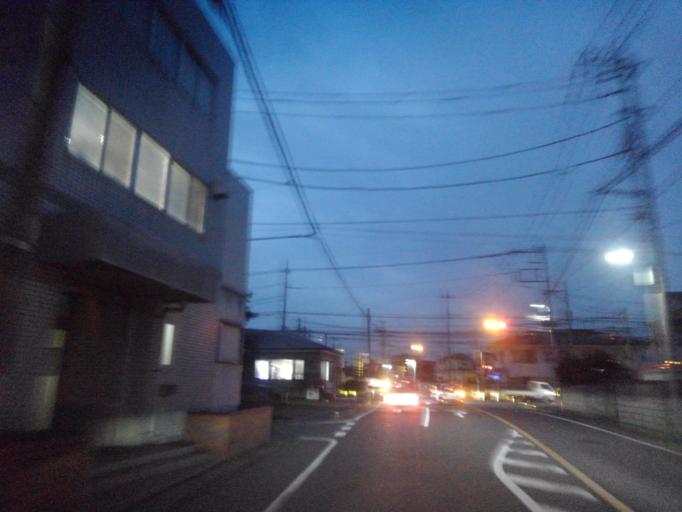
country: JP
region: Saitama
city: Tokorozawa
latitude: 35.8201
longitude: 139.4420
